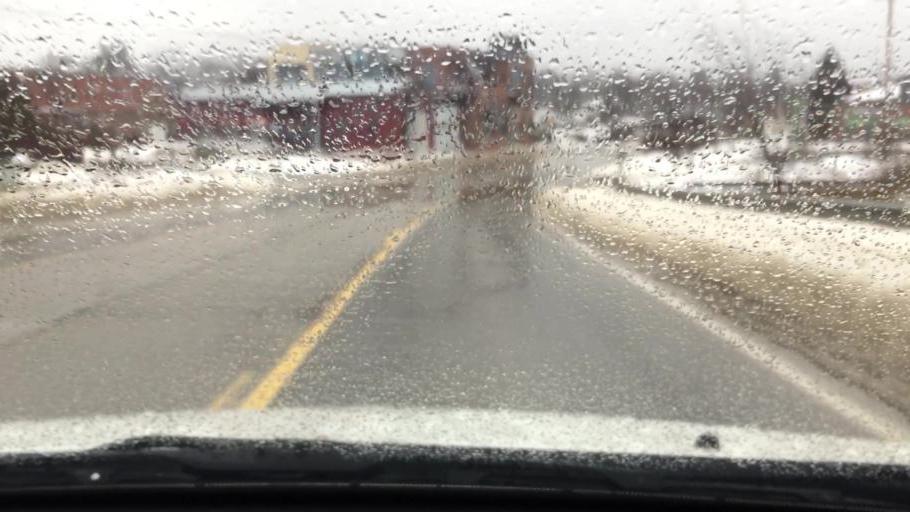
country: US
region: Michigan
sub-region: Charlevoix County
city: East Jordan
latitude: 45.1538
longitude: -85.1292
